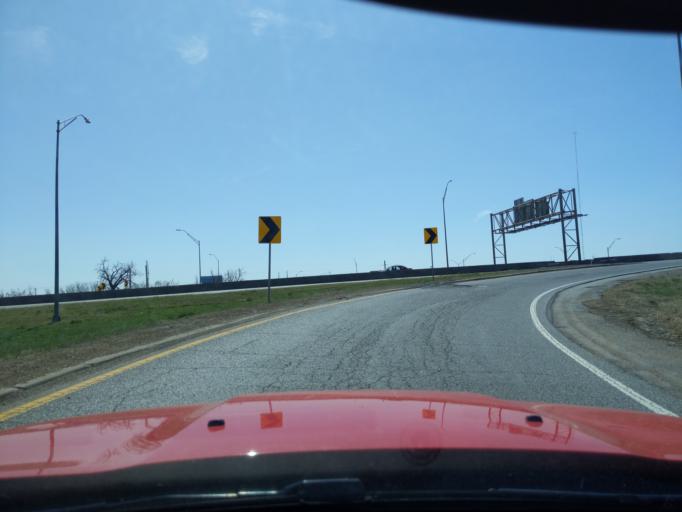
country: US
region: Oklahoma
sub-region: Cleveland County
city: Moore
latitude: 35.3921
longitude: -97.4938
